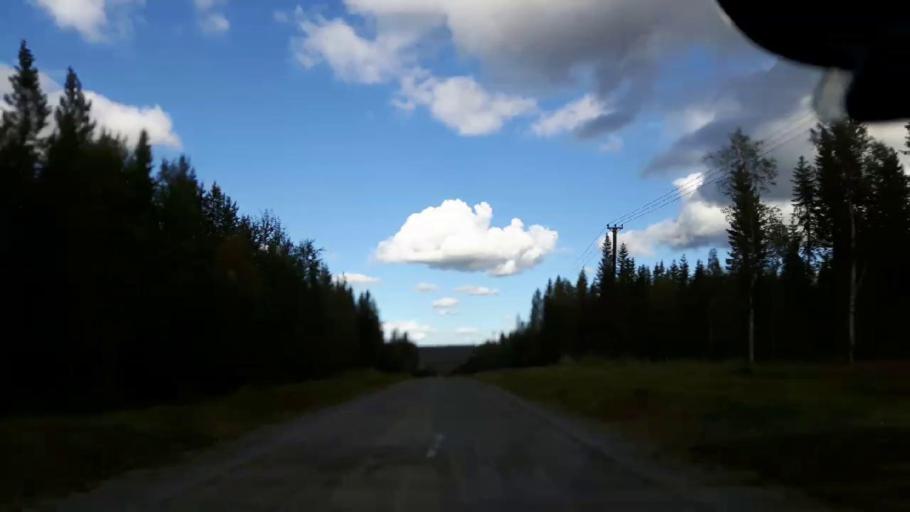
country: SE
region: Jaemtland
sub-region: Stroemsunds Kommun
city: Stroemsund
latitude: 63.4101
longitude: 15.7793
